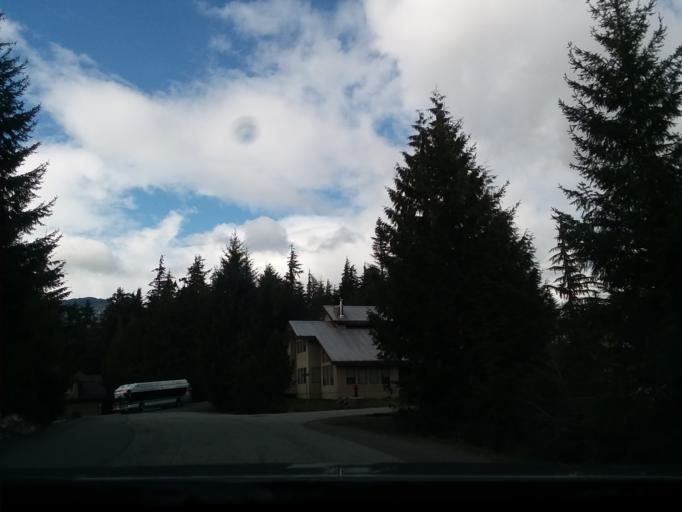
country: CA
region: British Columbia
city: Whistler
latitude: 50.1020
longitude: -122.9857
